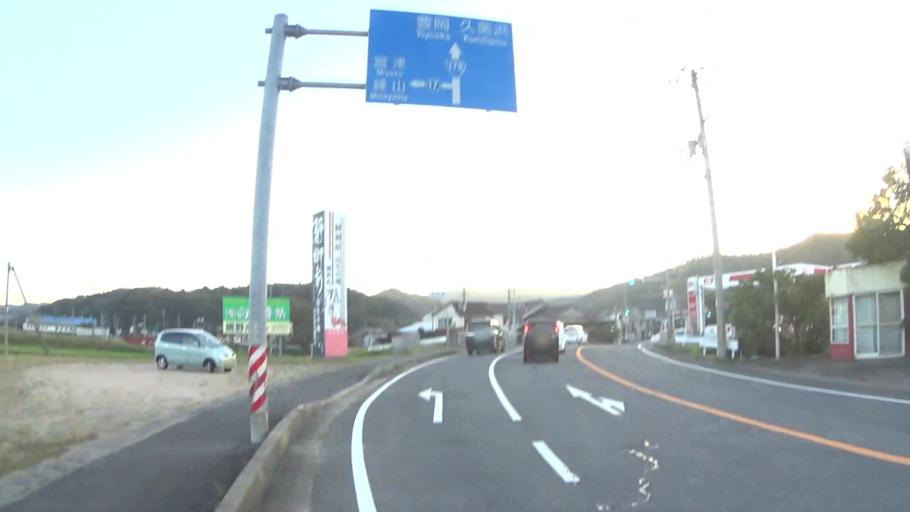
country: JP
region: Kyoto
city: Miyazu
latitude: 35.6695
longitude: 135.0276
